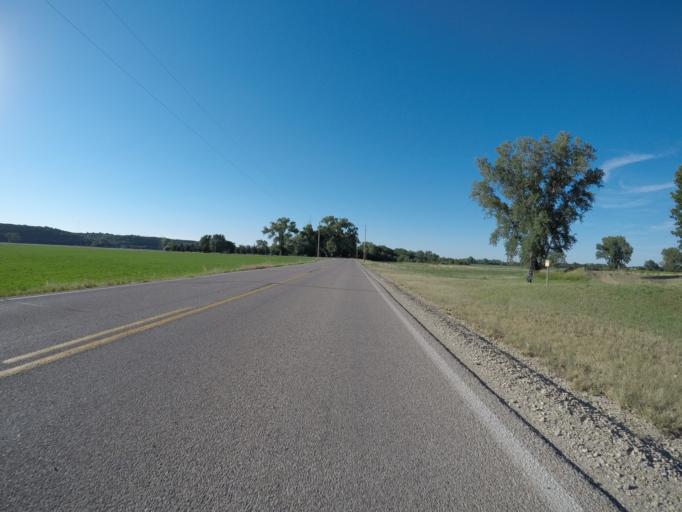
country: US
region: Kansas
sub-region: Riley County
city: Manhattan
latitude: 39.1492
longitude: -96.5886
